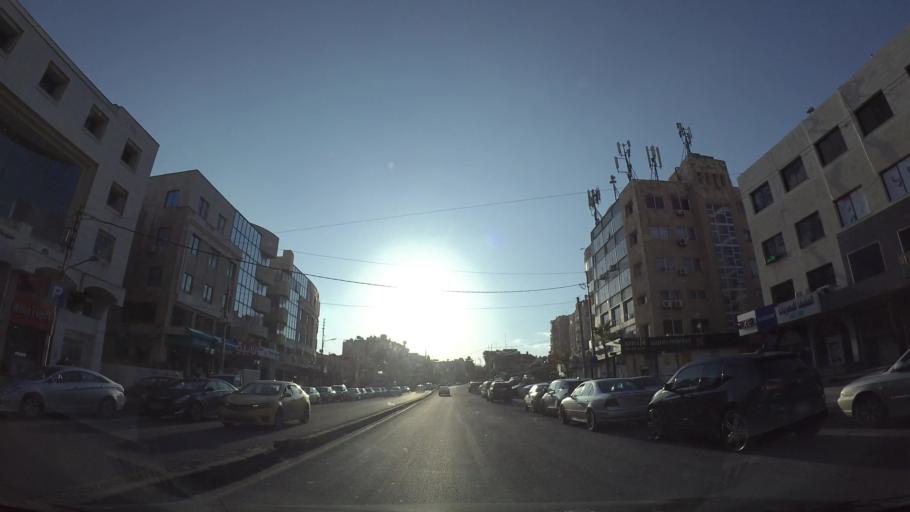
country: JO
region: Amman
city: Al Jubayhah
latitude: 31.9740
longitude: 35.8827
